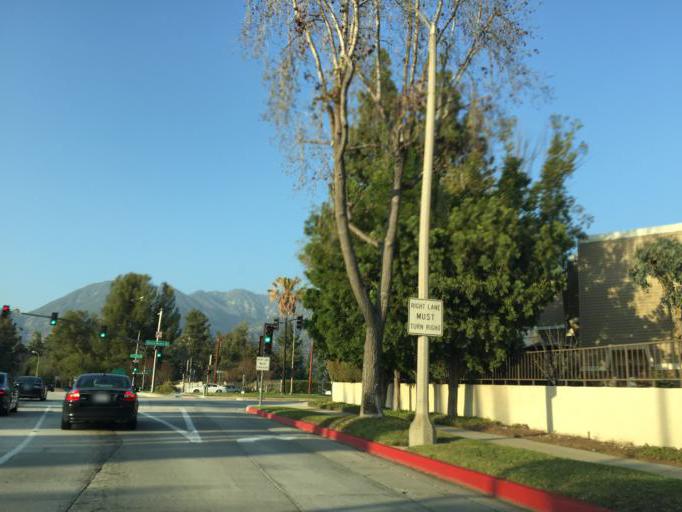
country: US
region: California
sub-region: Los Angeles County
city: East Pasadena
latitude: 34.1610
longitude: -118.0811
